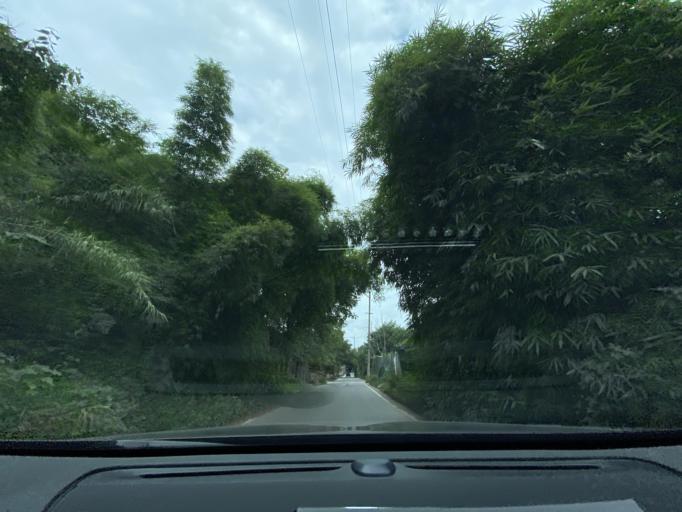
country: CN
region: Sichuan
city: Jiancheng
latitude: 30.4341
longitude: 104.5251
